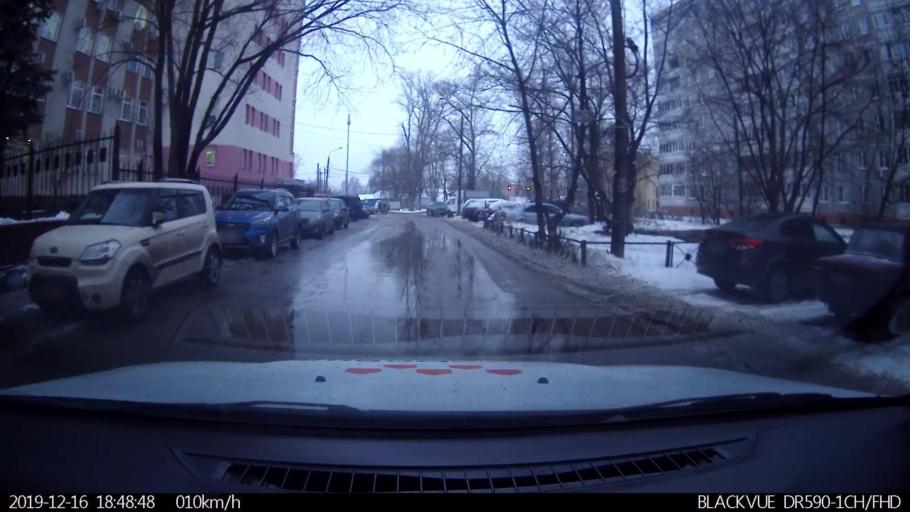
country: RU
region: Nizjnij Novgorod
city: Nizhniy Novgorod
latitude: 56.3044
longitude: 43.9316
